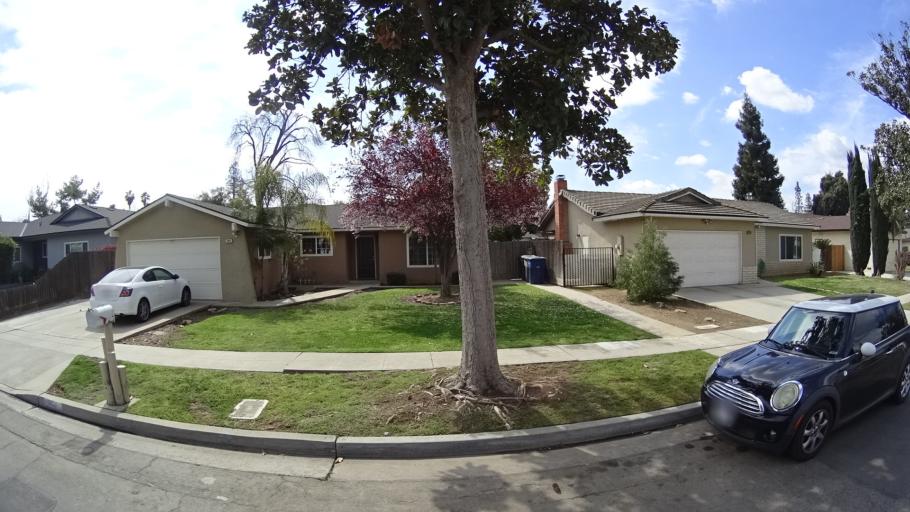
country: US
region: California
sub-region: Fresno County
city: Fresno
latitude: 36.8205
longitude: -119.8545
